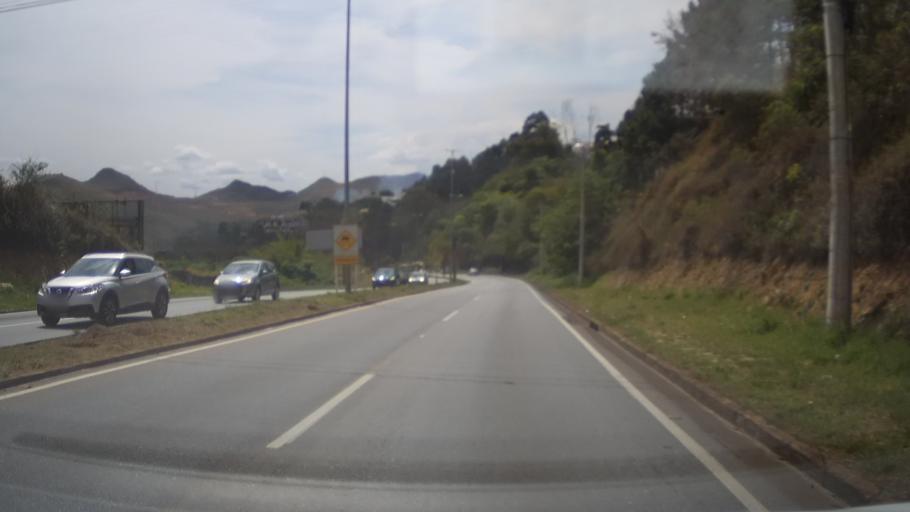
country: BR
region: Minas Gerais
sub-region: Belo Horizonte
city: Belo Horizonte
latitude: -19.9873
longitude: -43.9377
